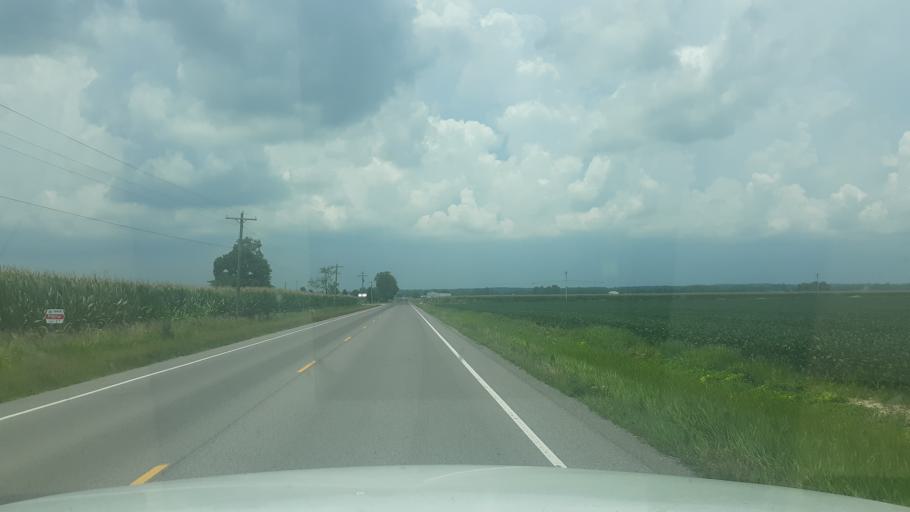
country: US
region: Illinois
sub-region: Saline County
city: Harrisburg
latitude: 37.8027
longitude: -88.5398
